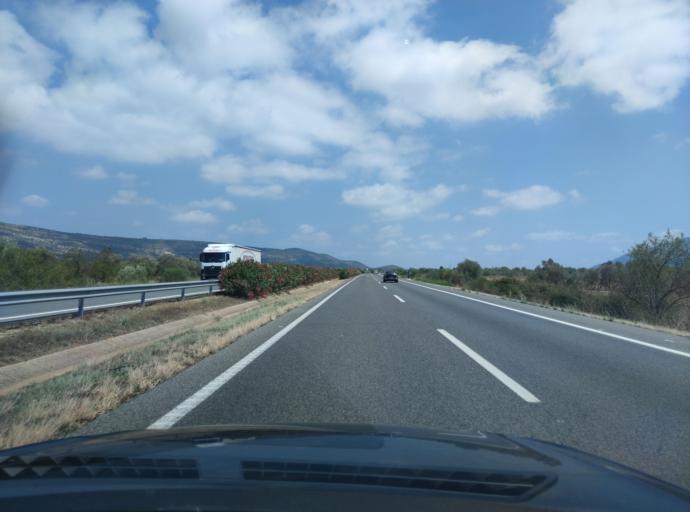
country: ES
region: Catalonia
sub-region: Provincia de Tarragona
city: Ulldecona
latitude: 40.6036
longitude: 0.4736
